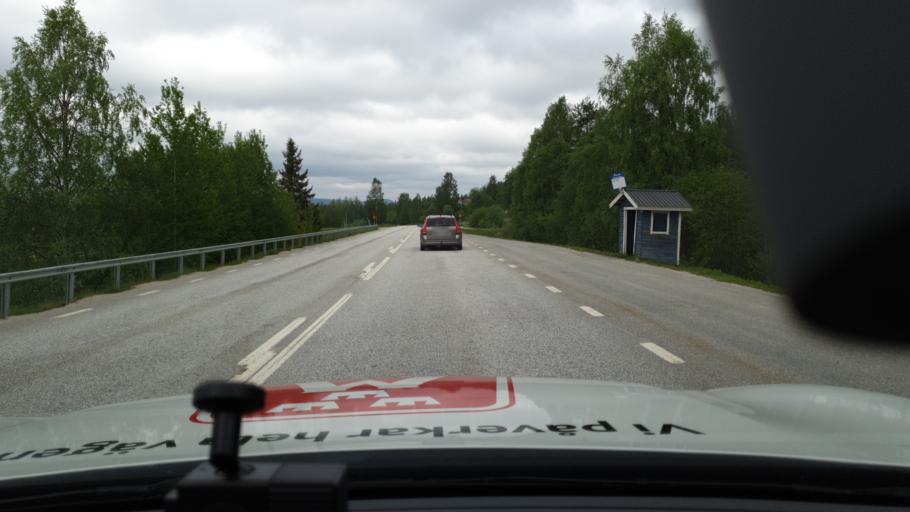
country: SE
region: Vaesterbotten
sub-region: Vannas Kommun
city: Vannasby
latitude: 64.1359
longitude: 19.9471
